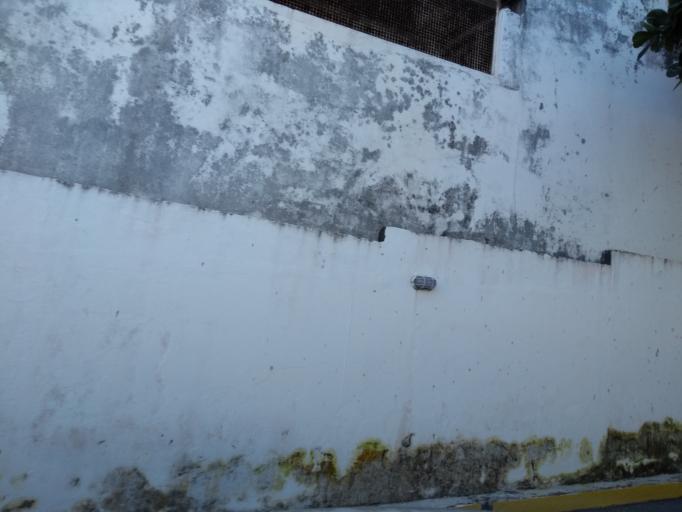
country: BR
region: Bahia
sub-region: Salvador
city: Salvador
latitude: -13.0083
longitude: -38.5246
